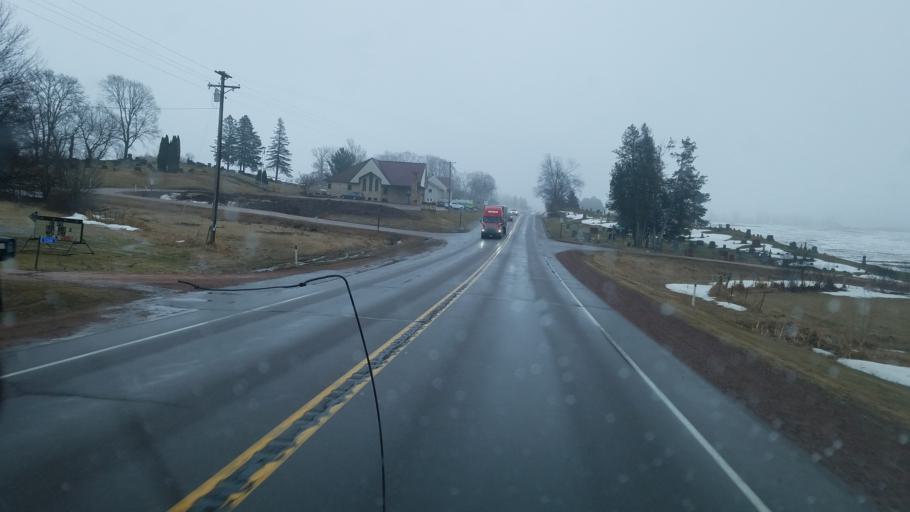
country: US
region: Wisconsin
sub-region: Wood County
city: Marshfield
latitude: 44.5989
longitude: -90.2797
